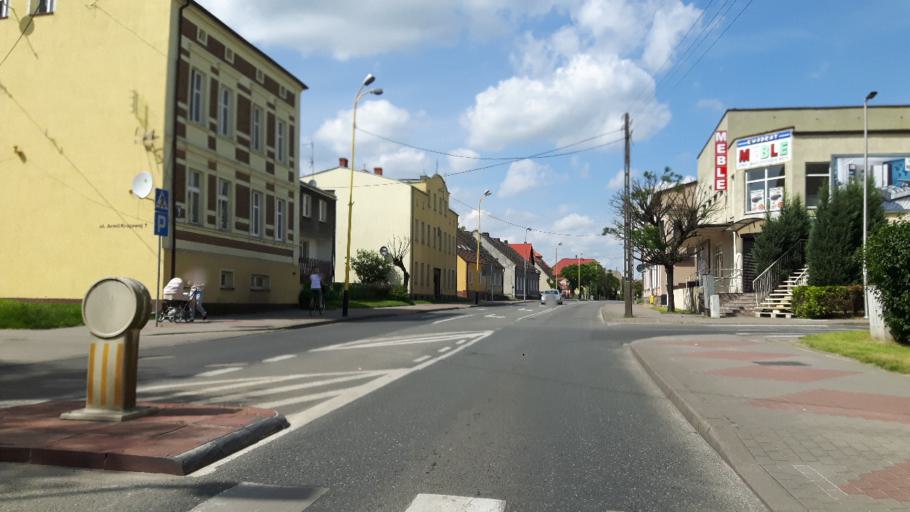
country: PL
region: West Pomeranian Voivodeship
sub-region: Powiat goleniowski
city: Nowogard
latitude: 53.6752
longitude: 15.1164
